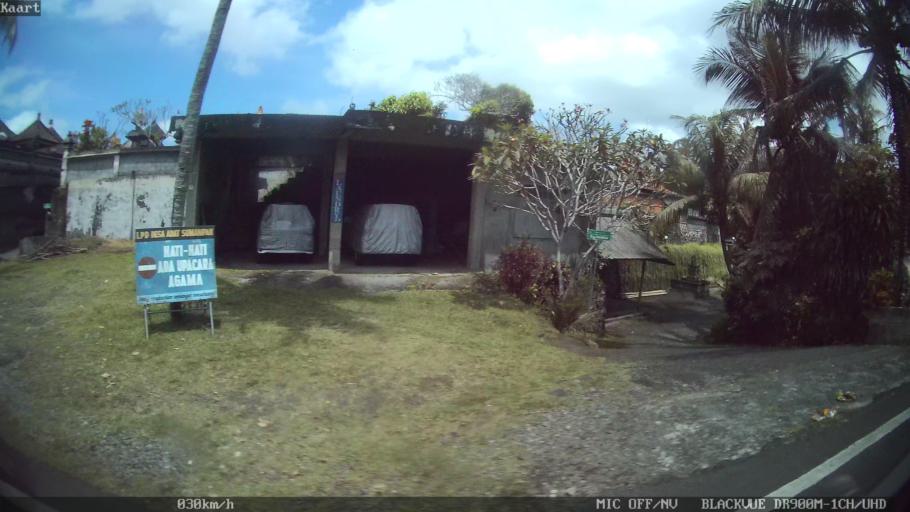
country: ID
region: Bali
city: Banjar Tebongkang
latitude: -8.5528
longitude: 115.2824
